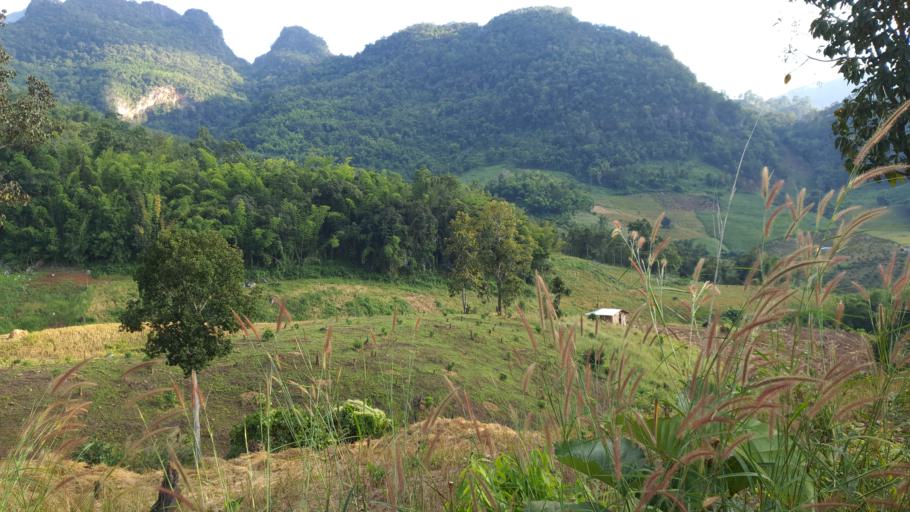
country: TH
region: Chiang Mai
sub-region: Amphoe Chiang Dao
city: Chiang Dao
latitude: 19.4047
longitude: 98.8311
